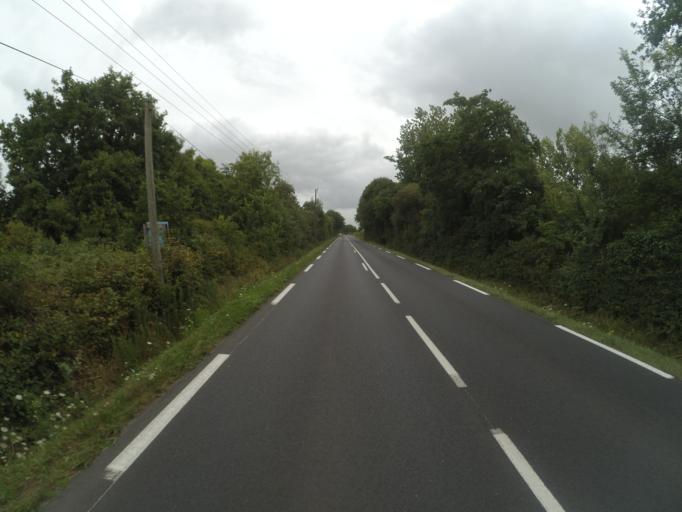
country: FR
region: Pays de la Loire
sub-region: Departement de la Vendee
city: Froidfond
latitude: 46.8653
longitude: -1.7774
